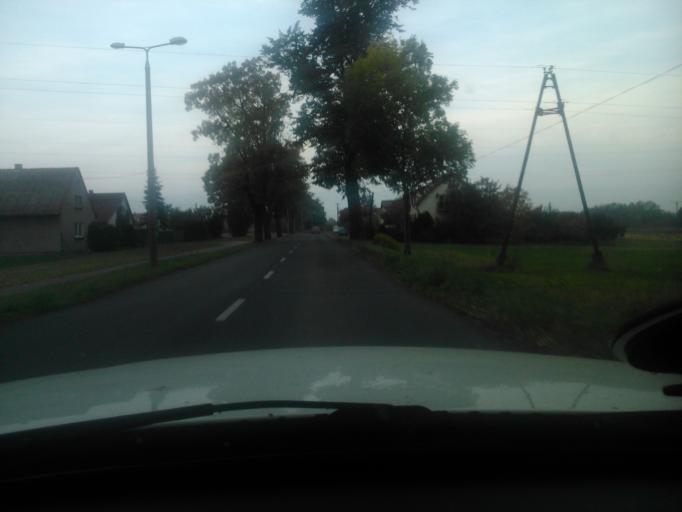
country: PL
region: Kujawsko-Pomorskie
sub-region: Powiat golubsko-dobrzynski
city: Kowalewo Pomorskie
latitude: 53.1606
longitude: 18.8793
